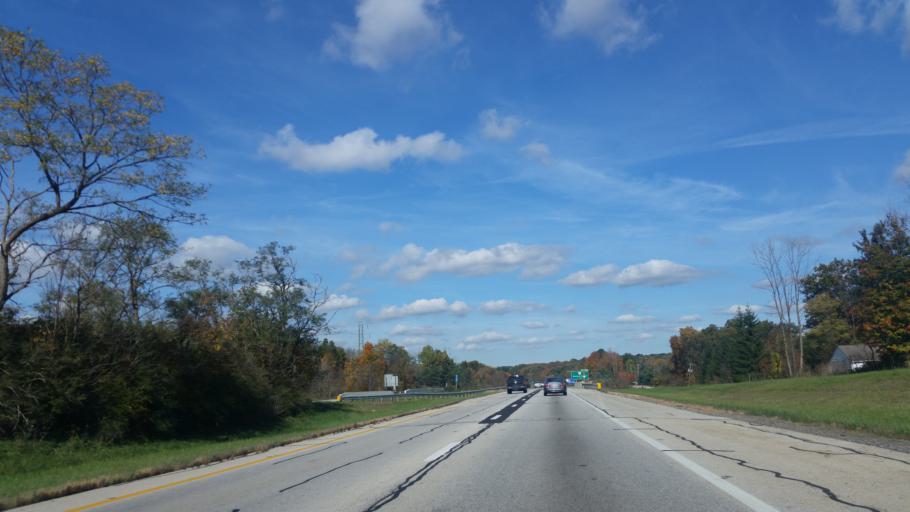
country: US
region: Ohio
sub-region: Summit County
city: Richfield
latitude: 41.2382
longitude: -81.6281
